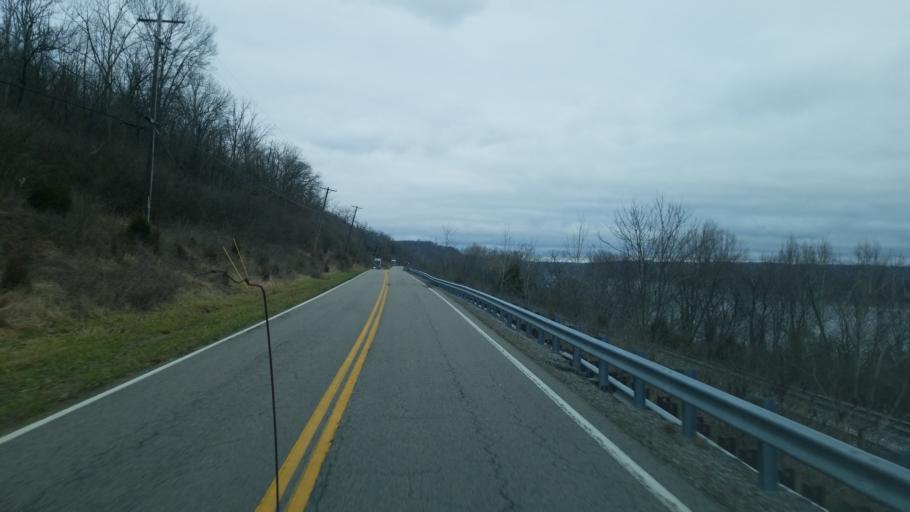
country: US
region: Ohio
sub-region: Clermont County
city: New Richmond
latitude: 38.9551
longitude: -84.2952
